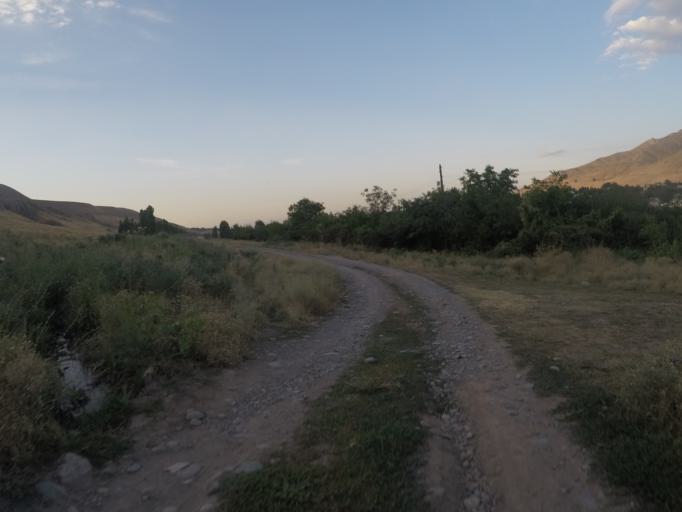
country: KG
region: Chuy
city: Bishkek
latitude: 42.7701
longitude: 74.6391
